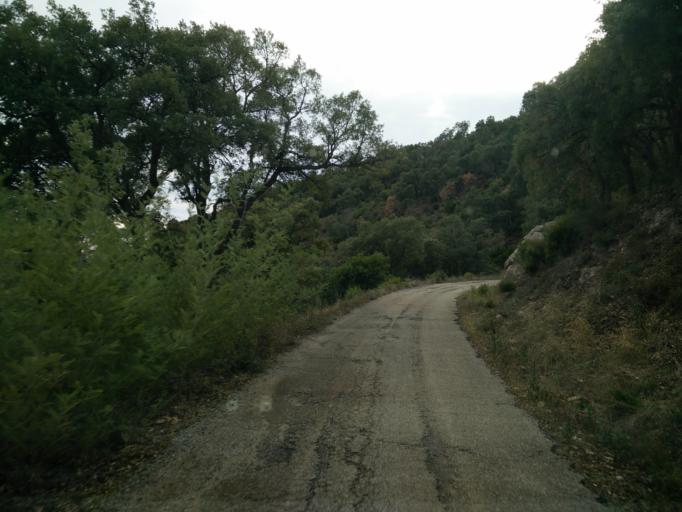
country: FR
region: Provence-Alpes-Cote d'Azur
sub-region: Departement du Var
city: Roquebrune-sur-Argens
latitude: 43.4014
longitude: 6.6206
